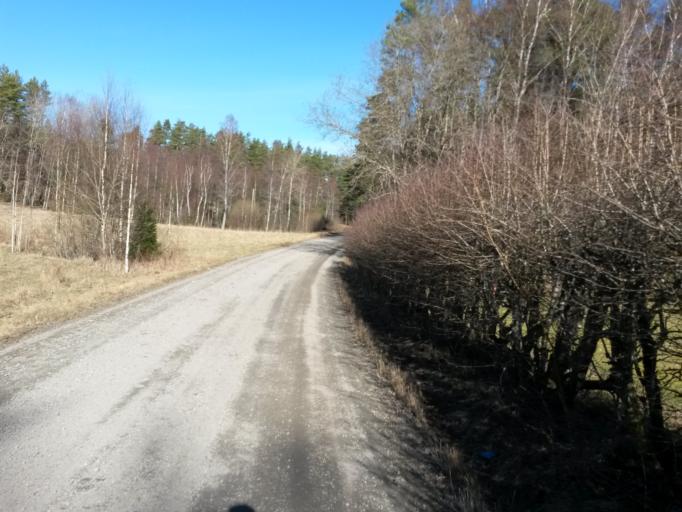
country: SE
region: Vaestra Goetaland
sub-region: Vargarda Kommun
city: Jonstorp
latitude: 57.9743
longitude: 12.7412
